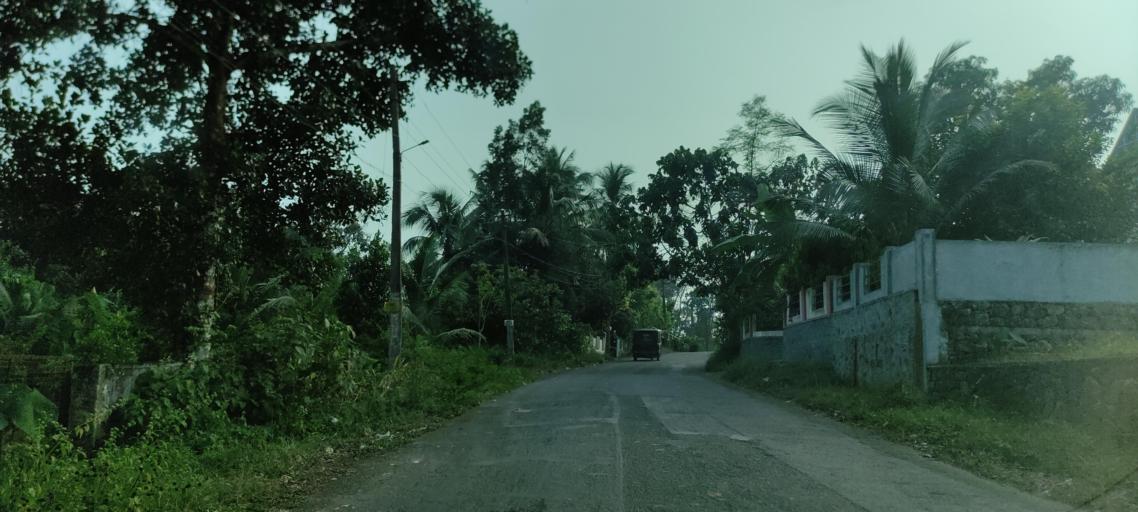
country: IN
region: Kerala
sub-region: Ernakulam
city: Piravam
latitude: 9.7918
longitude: 76.4995
